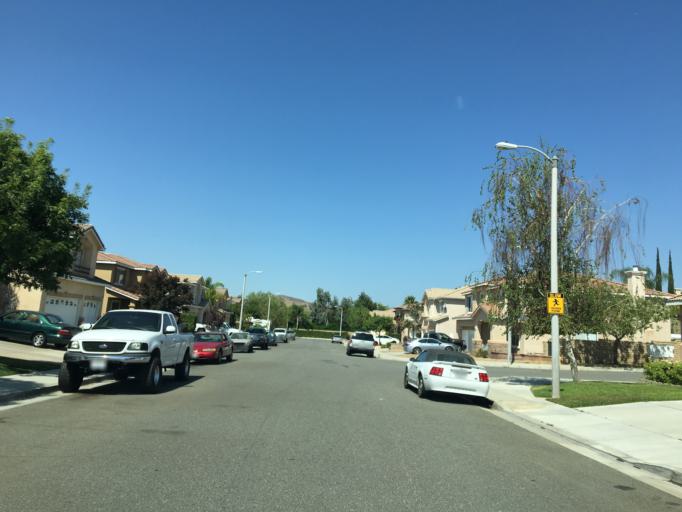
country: US
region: California
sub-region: Los Angeles County
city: Castaic
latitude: 34.4732
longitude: -118.6463
